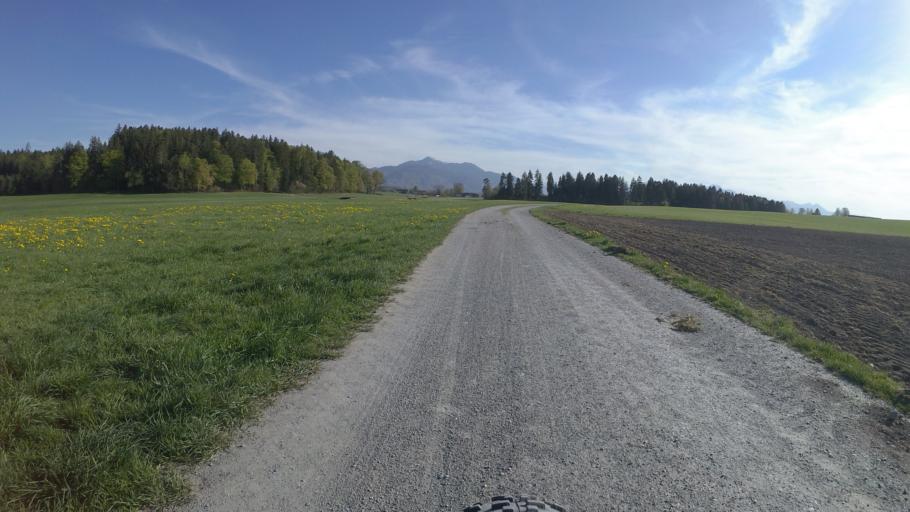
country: DE
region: Bavaria
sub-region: Upper Bavaria
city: Grabenstatt
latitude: 47.8673
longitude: 12.5389
